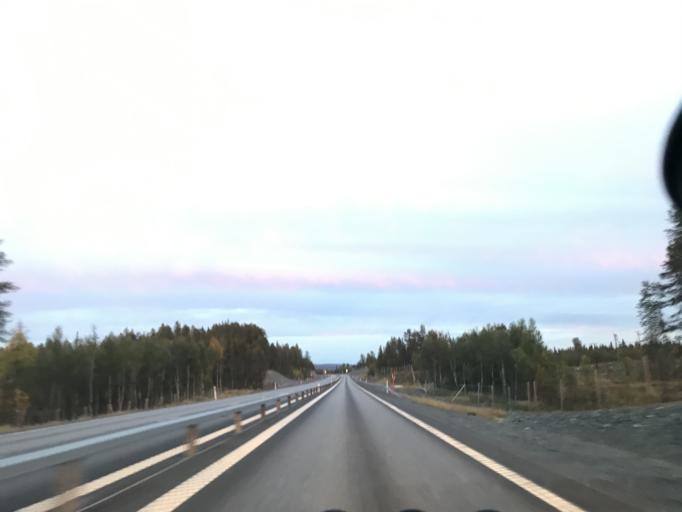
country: SE
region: Norrbotten
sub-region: Gallivare Kommun
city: Malmberget
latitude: 67.6801
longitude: 20.8785
